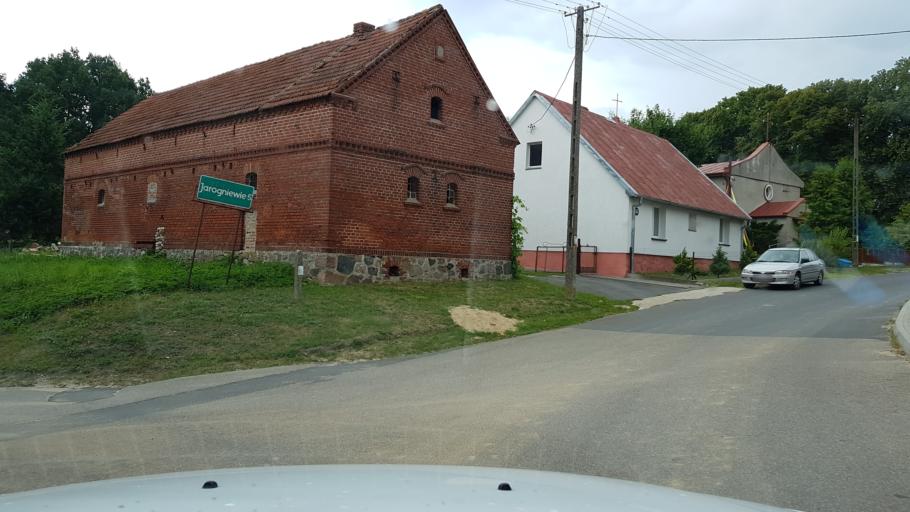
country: PL
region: West Pomeranian Voivodeship
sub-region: Powiat walecki
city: Walcz
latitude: 53.3532
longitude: 16.3961
